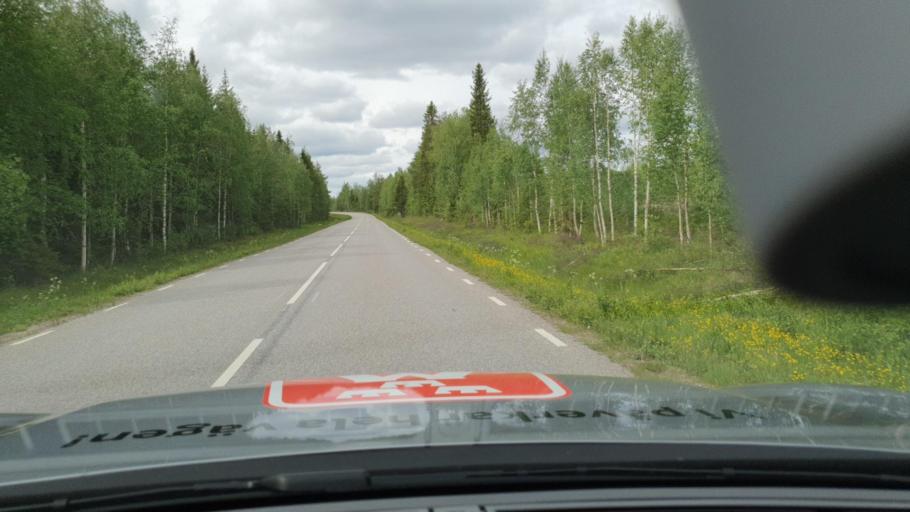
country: FI
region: Lapland
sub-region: Torniolaakso
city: Ylitornio
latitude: 66.0454
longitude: 23.6078
